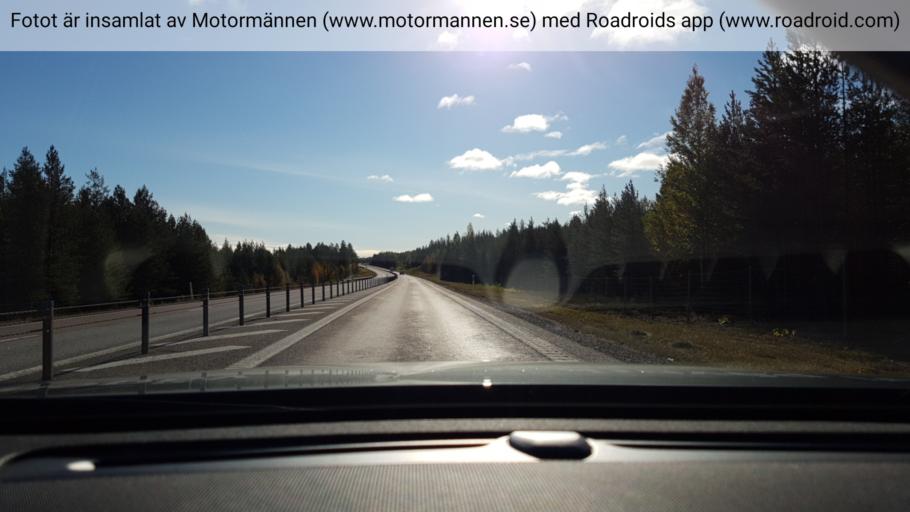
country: SE
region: Vaesterbotten
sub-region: Skelleftea Kommun
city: Soedra Bergsbyn
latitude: 64.6791
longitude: 21.0745
